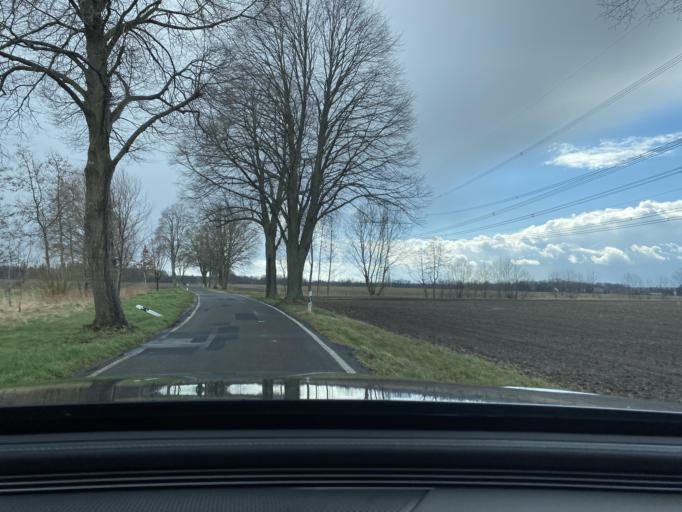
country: DE
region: Saxony
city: Uhyst
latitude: 51.3202
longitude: 14.4673
